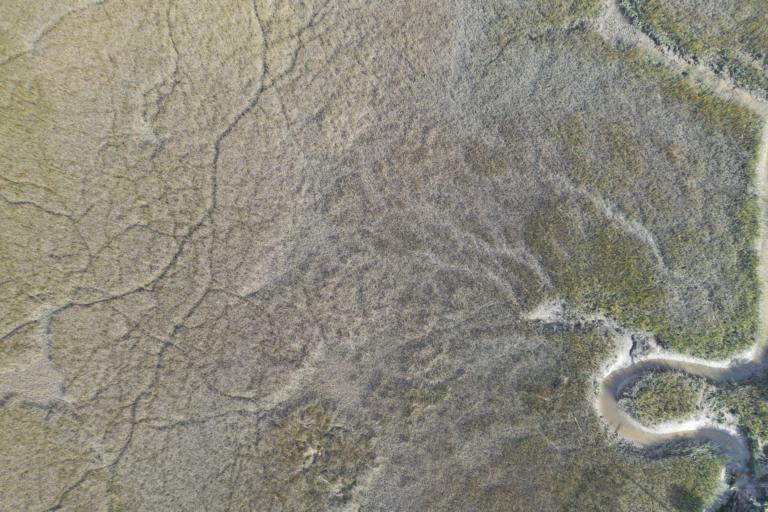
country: US
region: Georgia
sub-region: Chatham County
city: Montgomery
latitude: 31.9332
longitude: -81.0993
